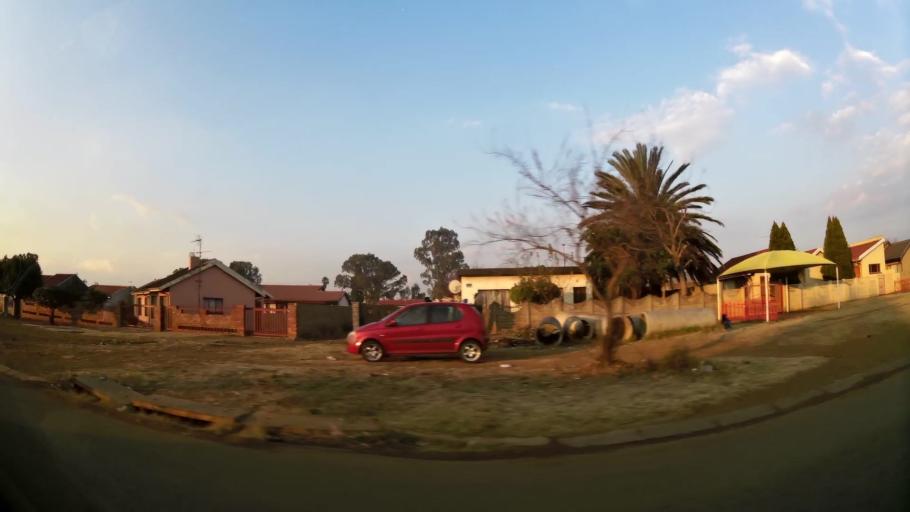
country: ZA
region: Gauteng
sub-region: City of Johannesburg Metropolitan Municipality
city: Orange Farm
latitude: -26.5416
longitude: 27.8846
